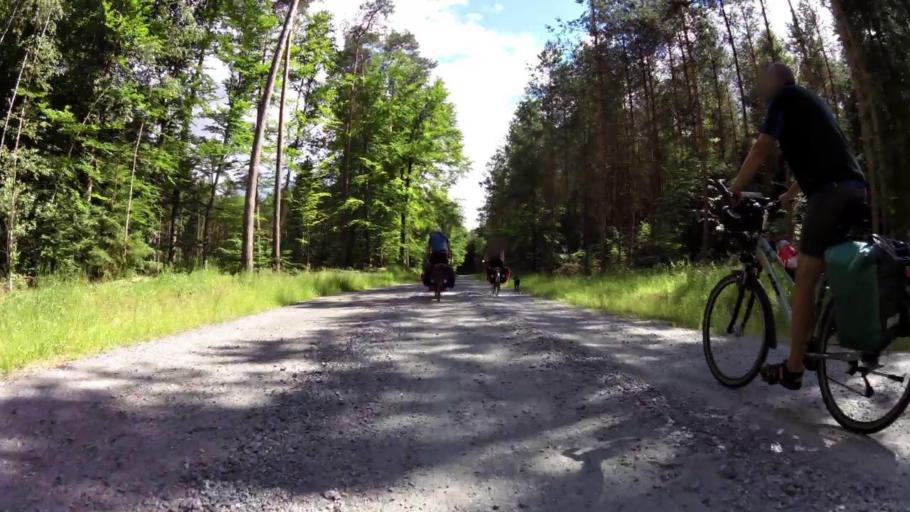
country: PL
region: West Pomeranian Voivodeship
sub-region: Powiat lobeski
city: Lobez
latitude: 53.6814
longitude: 15.5508
